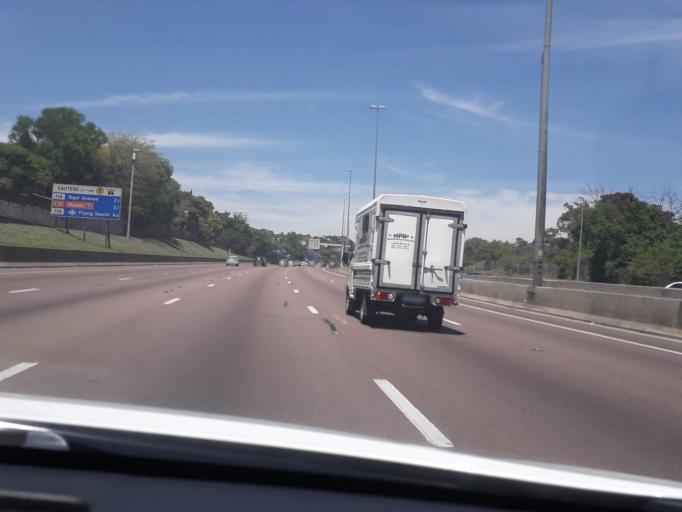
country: ZA
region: Gauteng
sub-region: City of Tshwane Metropolitan Municipality
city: Pretoria
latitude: -25.7898
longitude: 28.2690
